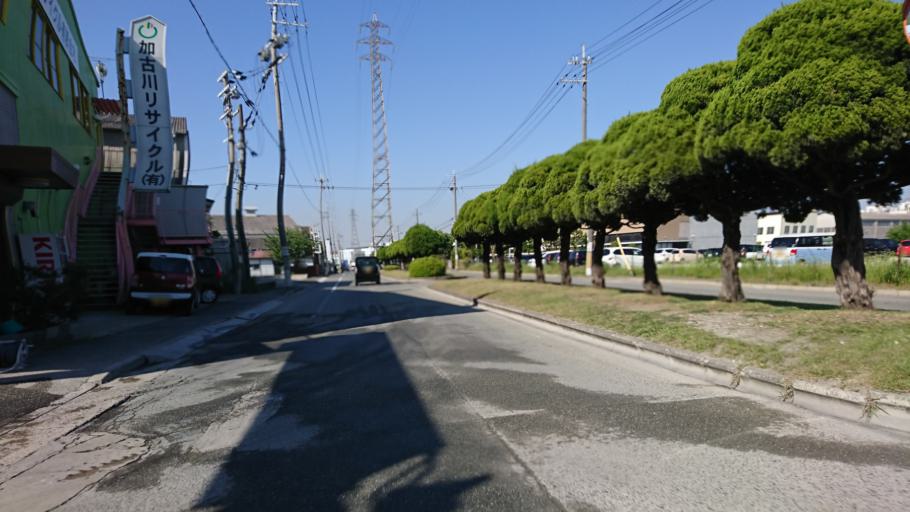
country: JP
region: Hyogo
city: Kakogawacho-honmachi
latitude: 34.7637
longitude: 134.8688
